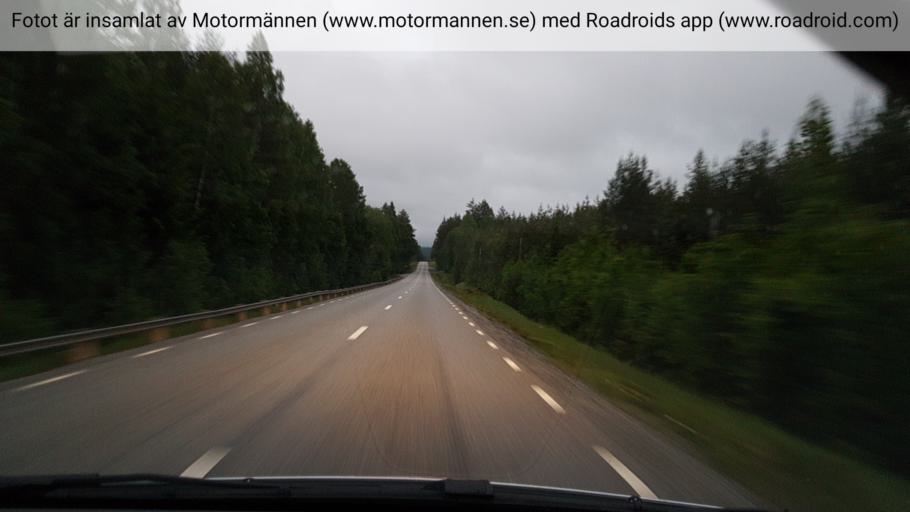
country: SE
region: Dalarna
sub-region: Smedjebackens Kommun
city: Smedjebacken
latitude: 59.9195
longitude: 15.4129
